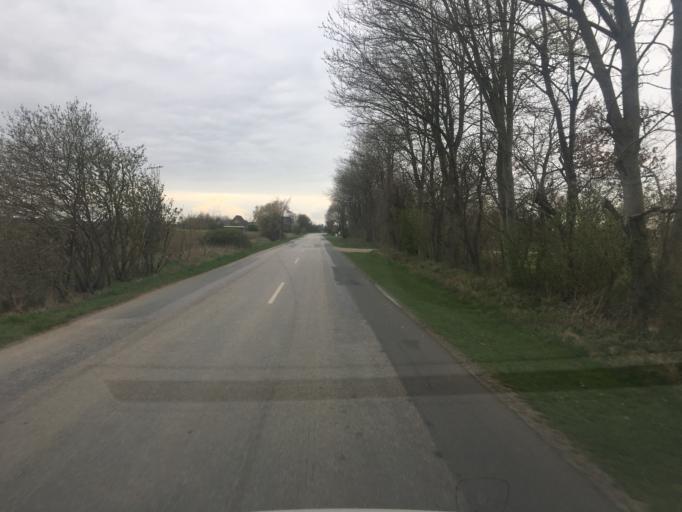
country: DK
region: South Denmark
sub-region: Aabenraa Kommune
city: Tinglev
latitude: 55.0276
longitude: 9.1676
